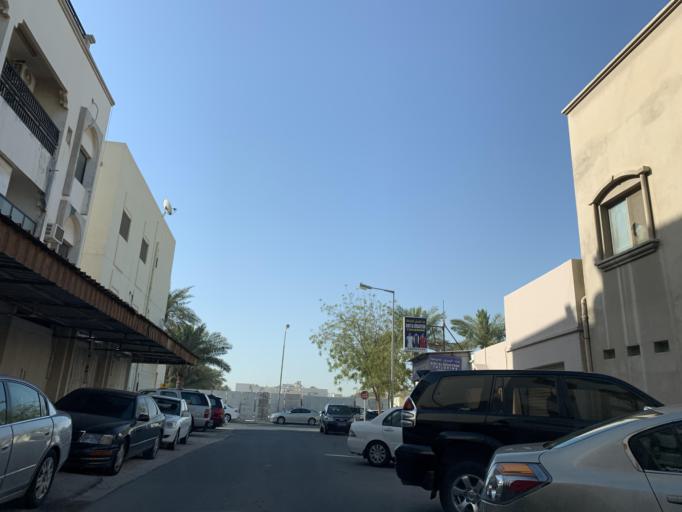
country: BH
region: Muharraq
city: Al Muharraq
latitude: 26.2647
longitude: 50.6069
